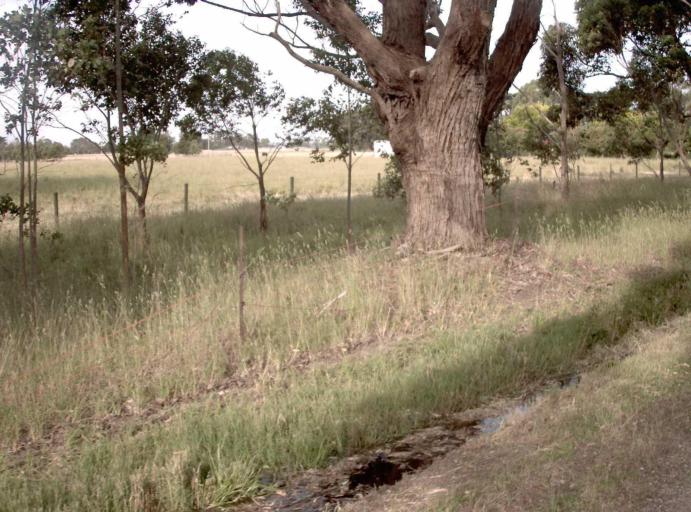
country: AU
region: Victoria
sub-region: Wellington
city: Heyfield
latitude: -38.0130
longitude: 146.6844
